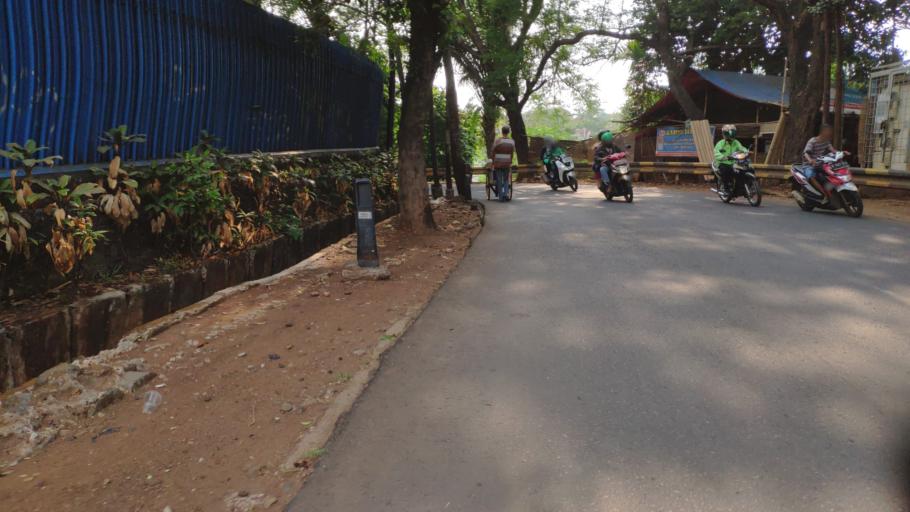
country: ID
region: West Java
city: Pamulang
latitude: -6.3109
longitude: 106.8098
